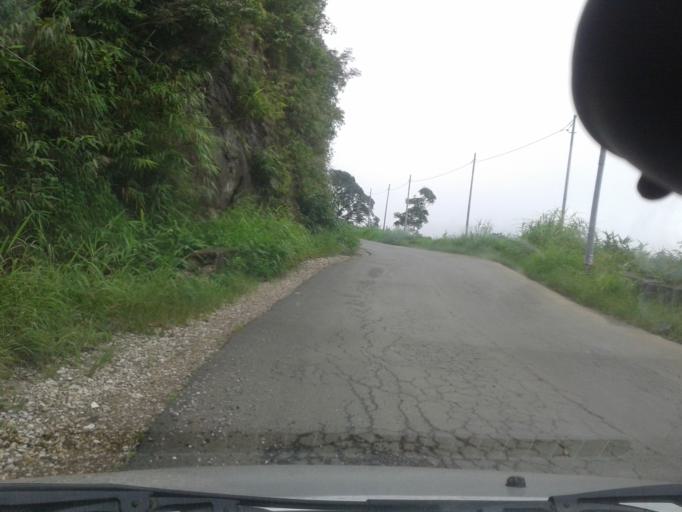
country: IN
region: Meghalaya
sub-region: East Khasi Hills
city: Cherrapunji
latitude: 25.2077
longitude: 91.7400
